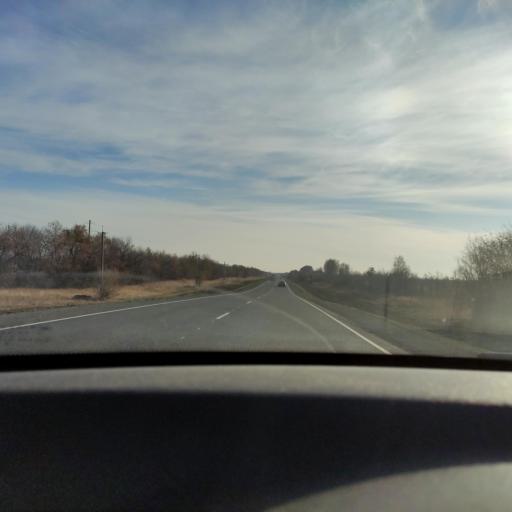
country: RU
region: Samara
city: Krasnoarmeyskoye
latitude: 52.8216
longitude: 50.0091
